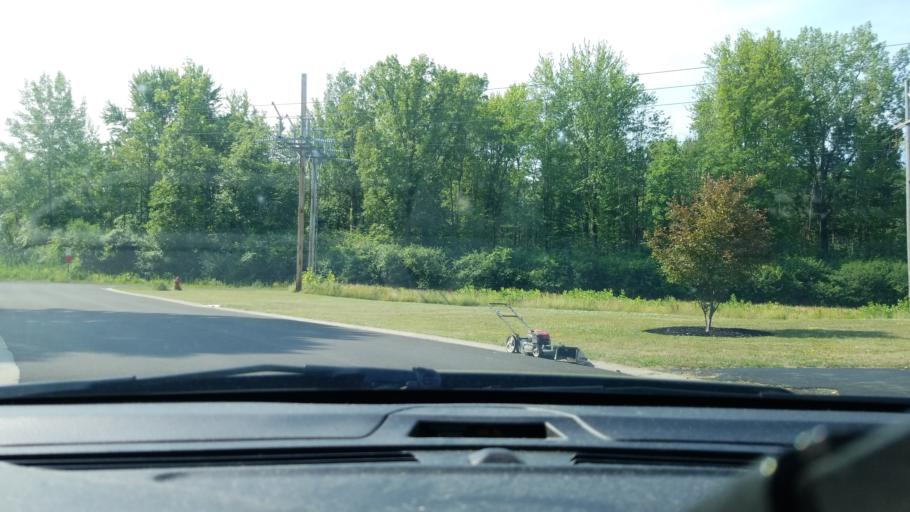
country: US
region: New York
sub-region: Onondaga County
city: East Syracuse
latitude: 43.0970
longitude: -76.0707
